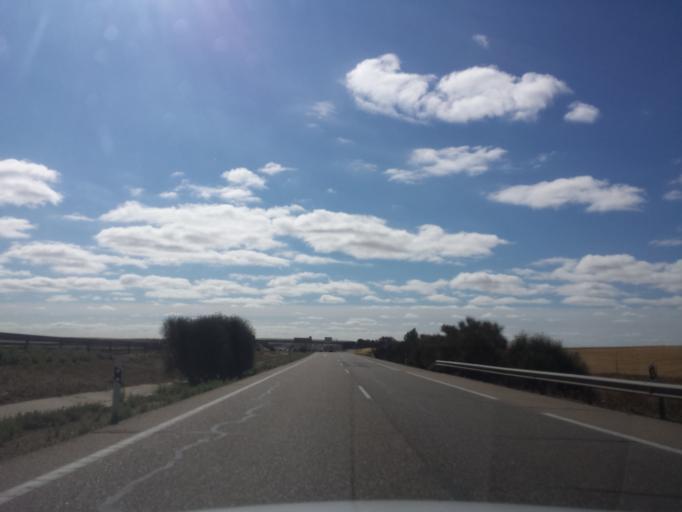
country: ES
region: Castille and Leon
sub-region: Provincia de Zamora
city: Cerecinos de Campos
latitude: 41.9094
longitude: -5.5010
